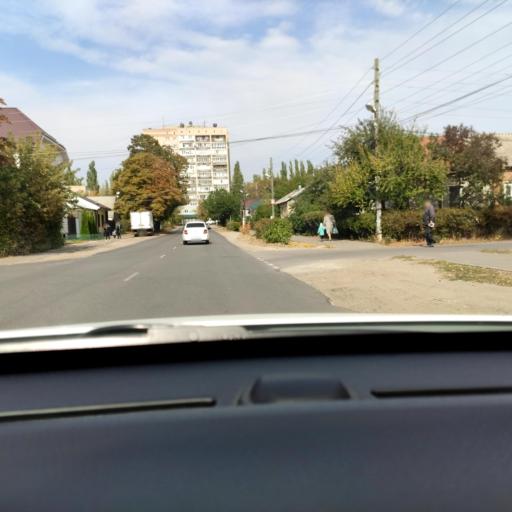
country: RU
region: Voronezj
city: Voronezh
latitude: 51.6969
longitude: 39.1897
